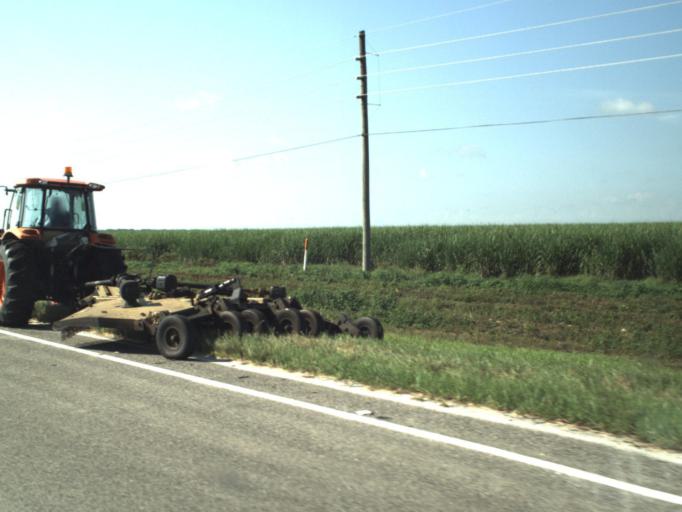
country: US
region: Florida
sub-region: Palm Beach County
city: Belle Glade Camp
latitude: 26.5350
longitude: -80.6931
